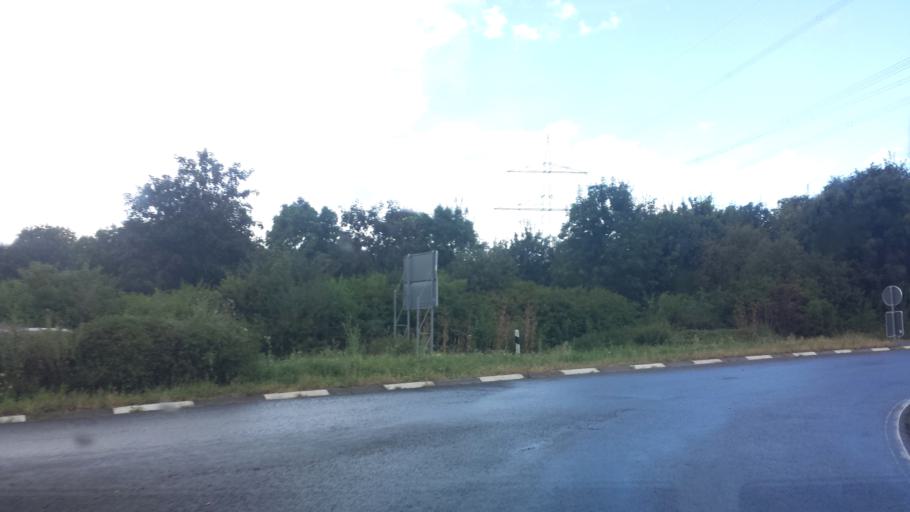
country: DE
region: Rheinland-Pfalz
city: Osthofen
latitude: 49.6771
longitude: 8.3306
